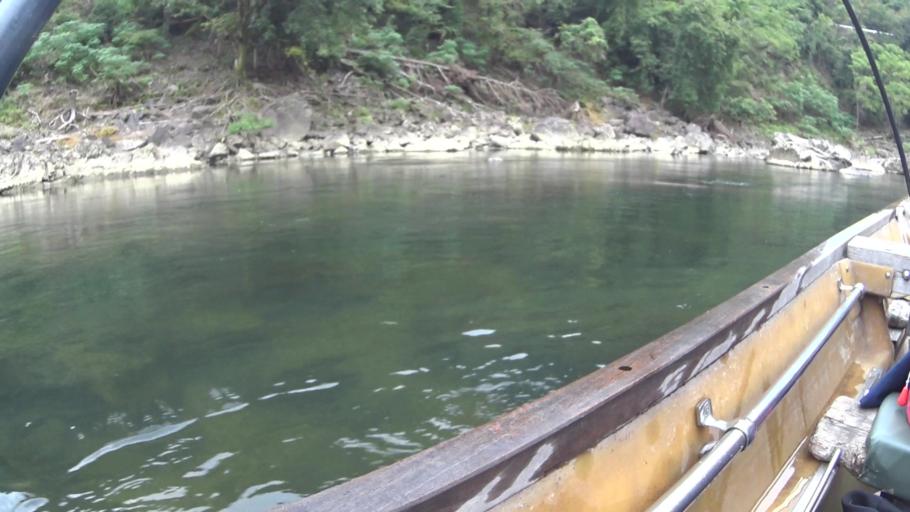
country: JP
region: Kyoto
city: Kameoka
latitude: 35.0237
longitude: 135.6203
